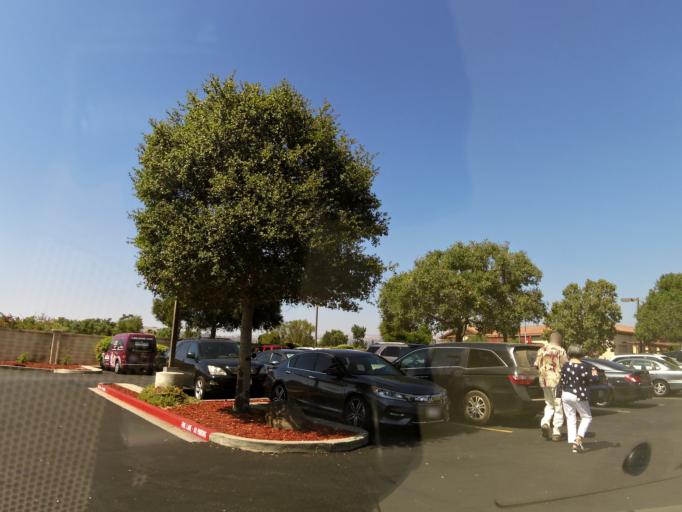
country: US
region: California
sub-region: Santa Clara County
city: Morgan Hill
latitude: 37.1304
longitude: -121.6390
